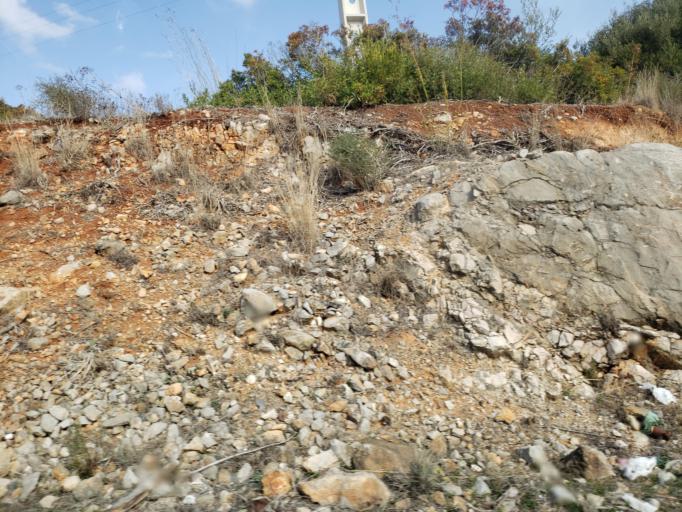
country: PT
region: Faro
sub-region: Portimao
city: Alvor
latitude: 37.1797
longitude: -8.5827
